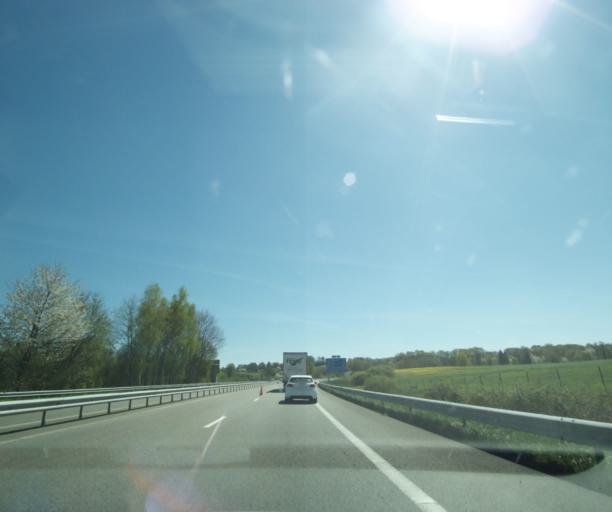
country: FR
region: Limousin
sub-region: Departement de la Haute-Vienne
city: Saint-Germain-les-Belles
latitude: 45.6183
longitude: 1.4484
